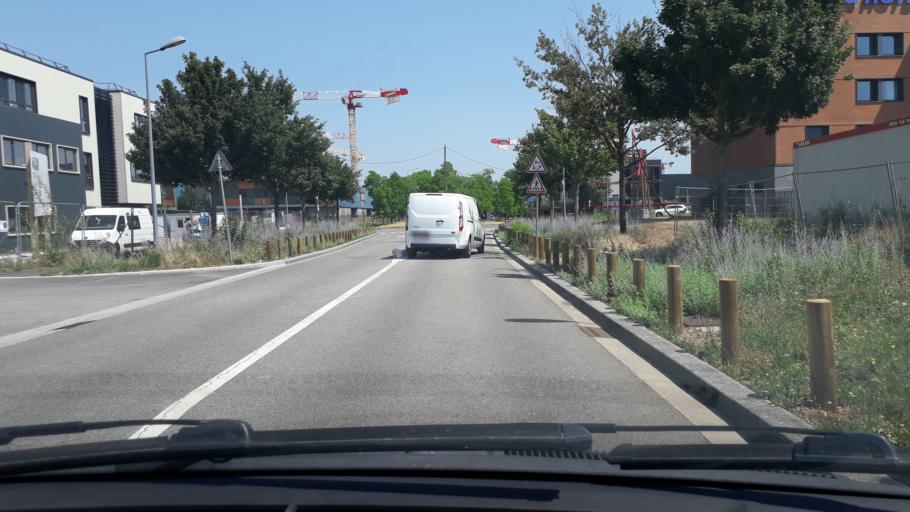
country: FR
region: Rhone-Alpes
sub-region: Departement du Rhone
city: Jonage
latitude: 45.7687
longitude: 5.0353
